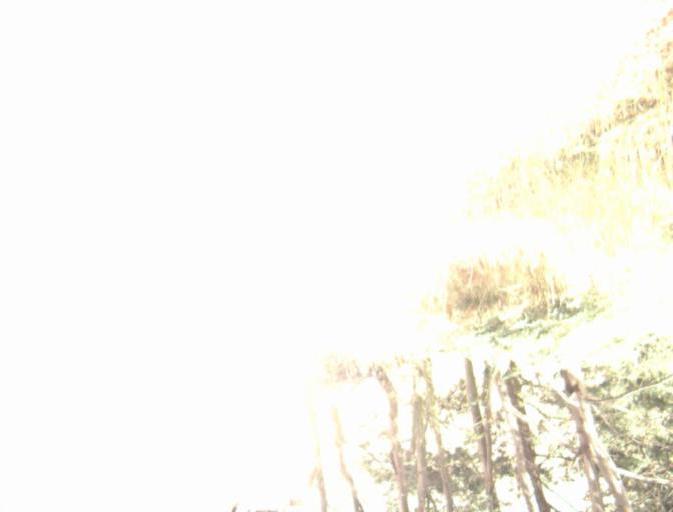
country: AU
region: Tasmania
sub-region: Dorset
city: Scottsdale
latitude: -41.4459
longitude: 147.5871
